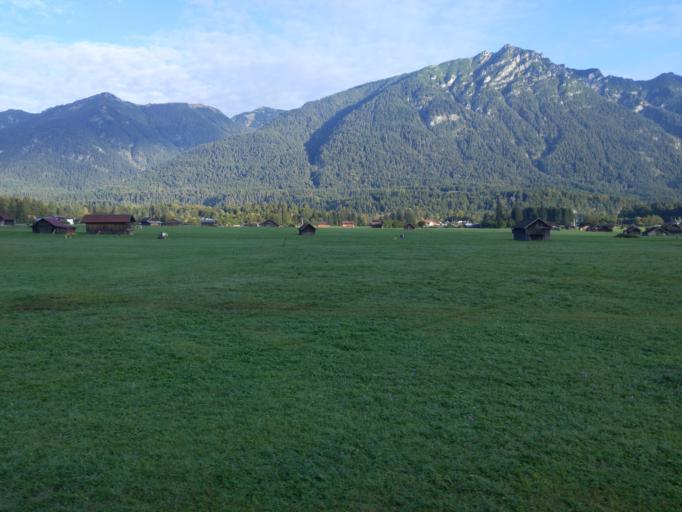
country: DE
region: Bavaria
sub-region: Upper Bavaria
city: Grainau
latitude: 47.4695
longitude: 11.0555
